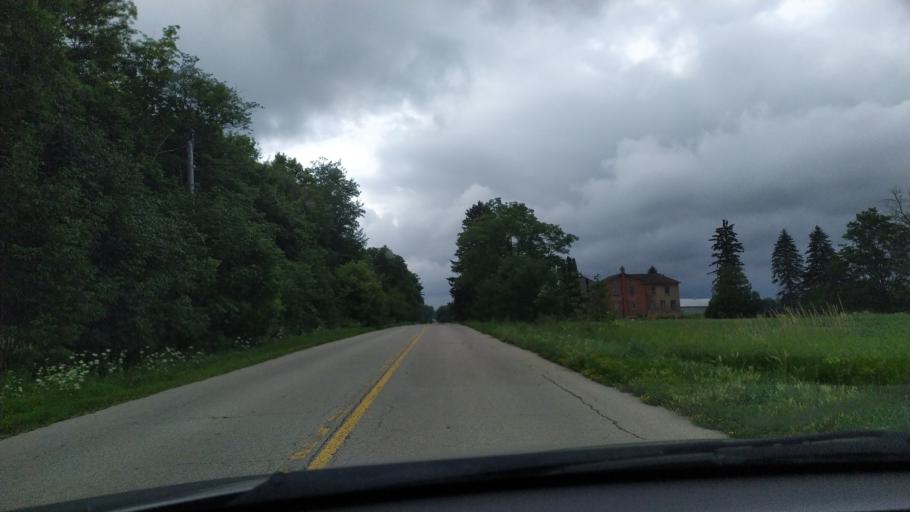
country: CA
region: Ontario
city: Kitchener
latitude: 43.3305
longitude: -80.6596
